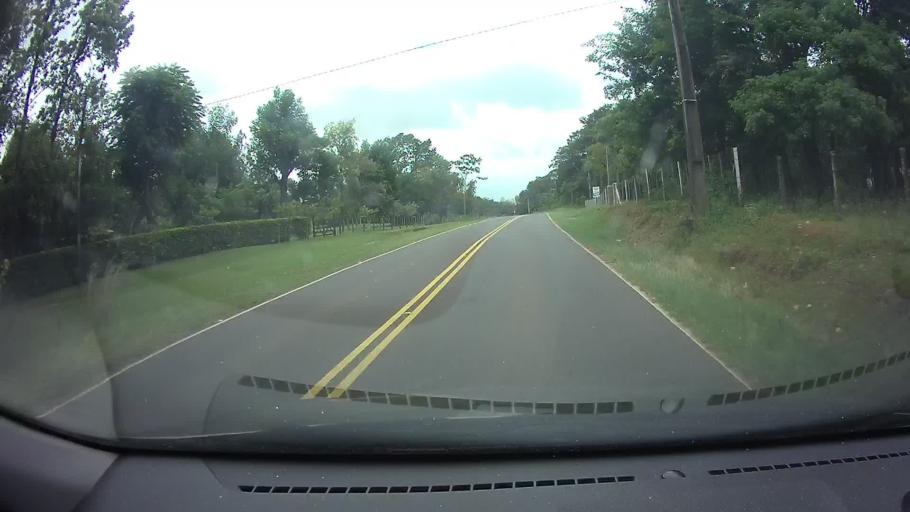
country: PY
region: Central
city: Nueva Italia
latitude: -25.6097
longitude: -57.4301
